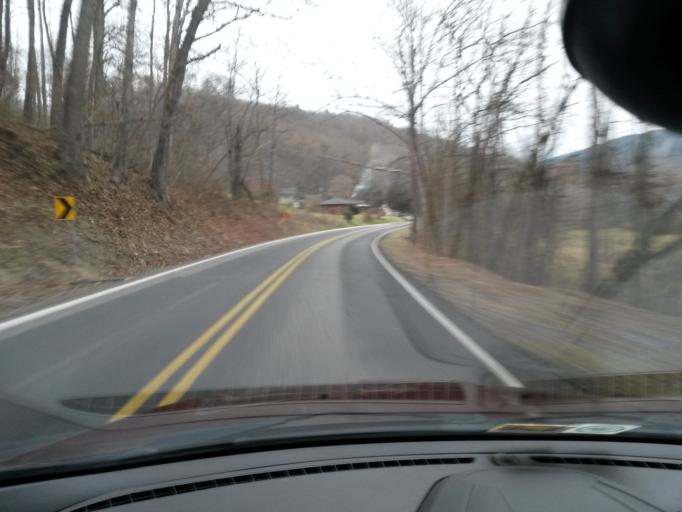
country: US
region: Virginia
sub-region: Bath County
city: Warm Springs
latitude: 38.0016
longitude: -79.5576
